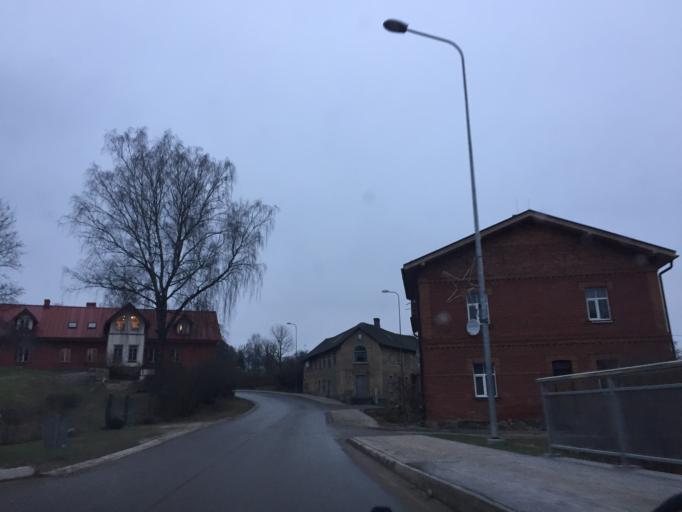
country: LV
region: Raunas
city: Rauna
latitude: 57.3333
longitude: 25.6088
